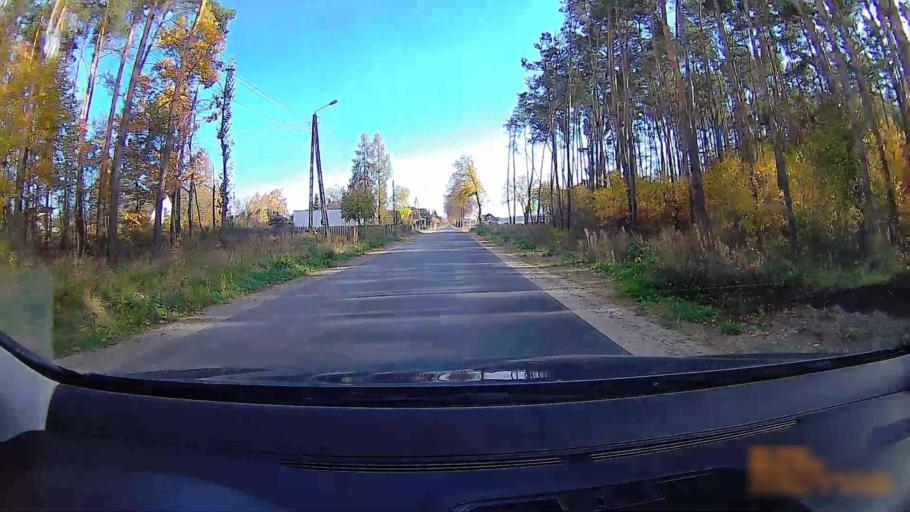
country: PL
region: Greater Poland Voivodeship
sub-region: Powiat ostrzeszowski
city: Doruchow
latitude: 51.4051
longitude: 18.0249
